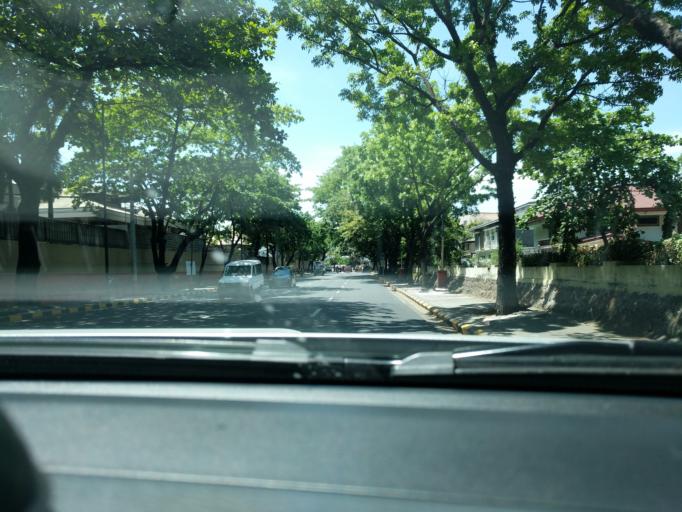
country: PH
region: Metro Manila
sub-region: Pasig
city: Pasig City
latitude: 14.5809
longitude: 121.0707
